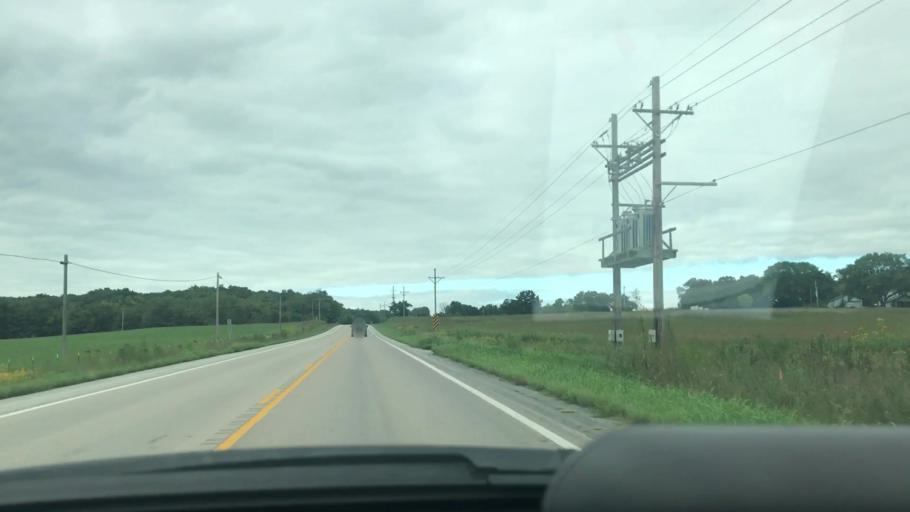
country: US
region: Missouri
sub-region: Hickory County
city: Hermitage
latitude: 37.8653
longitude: -93.1789
